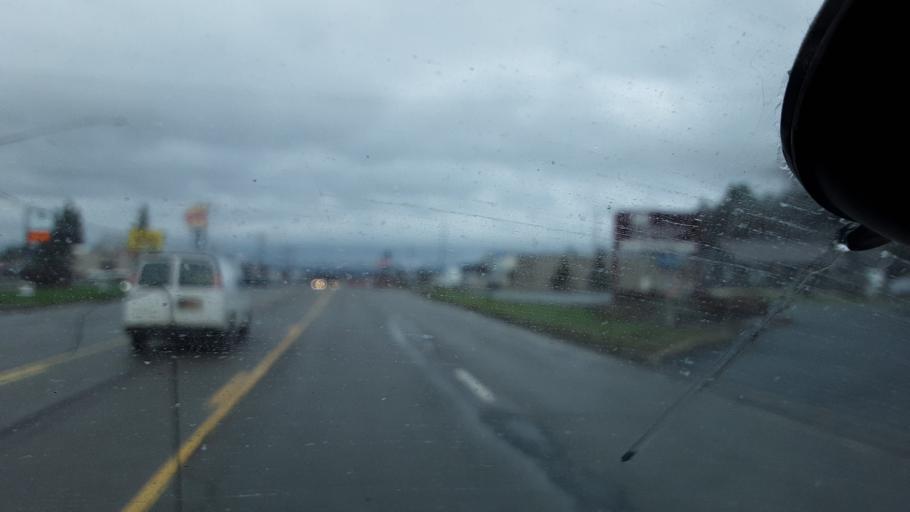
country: US
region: New York
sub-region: Cattaraugus County
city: Yorkshire
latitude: 42.5280
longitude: -78.4785
